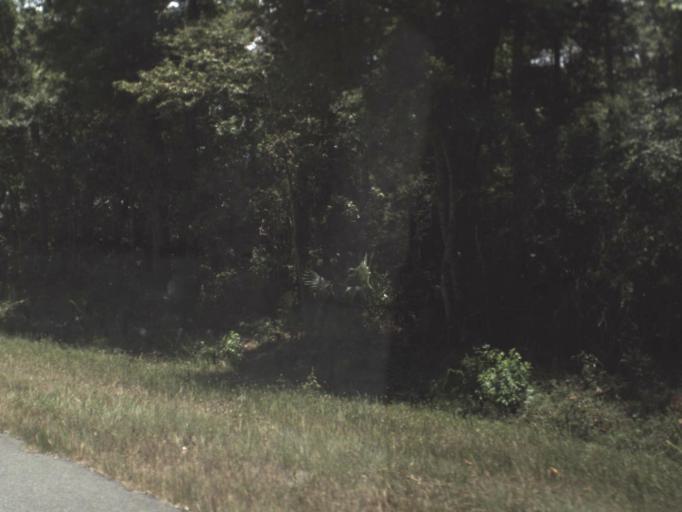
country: US
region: Florida
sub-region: Leon County
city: Woodville
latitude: 30.1443
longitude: -83.9486
